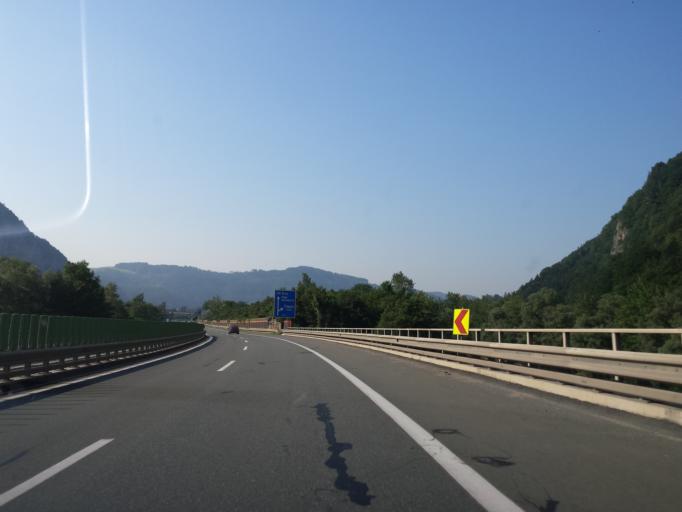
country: AT
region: Styria
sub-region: Politischer Bezirk Graz-Umgebung
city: Peggau
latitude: 47.2190
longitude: 15.3362
